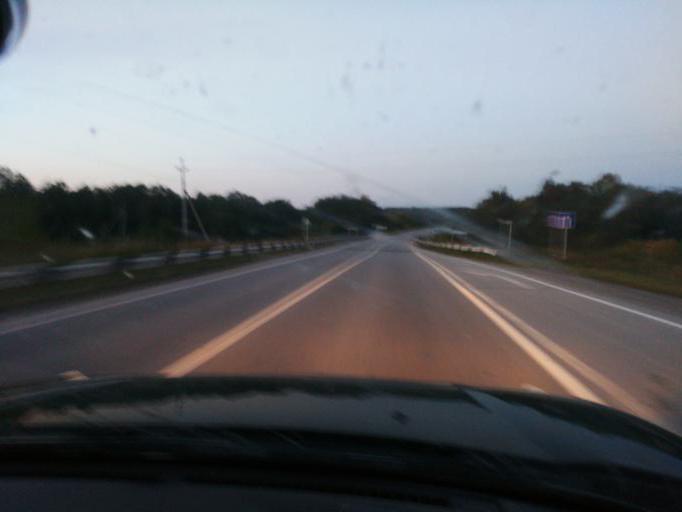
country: RU
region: Perm
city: Verkhnechusovskiye Gorodki
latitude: 58.2661
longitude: 57.3434
